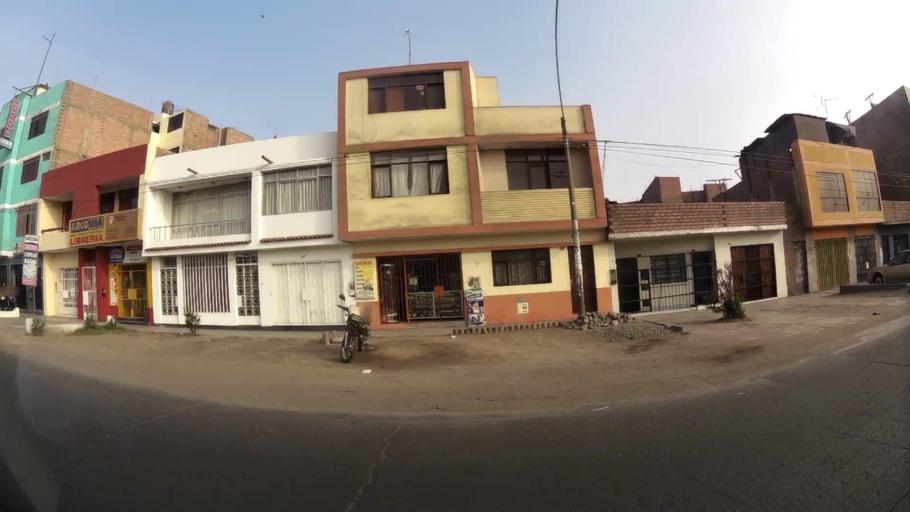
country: PE
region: Callao
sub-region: Callao
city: Callao
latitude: -12.0294
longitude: -77.0795
